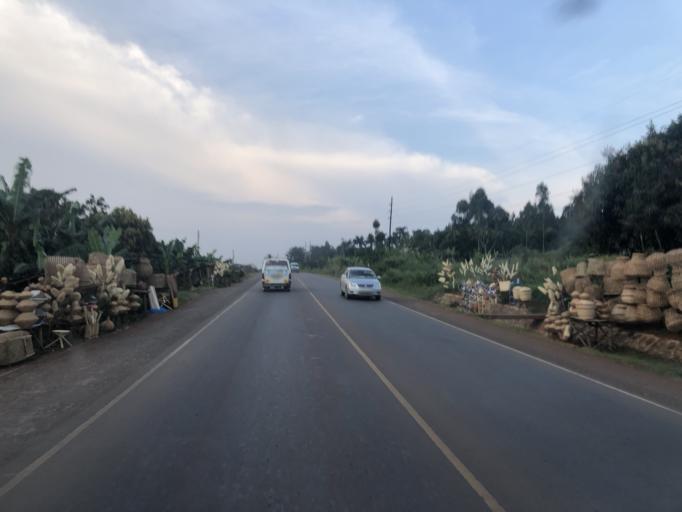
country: UG
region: Central Region
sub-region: Mpigi District
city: Mpigi
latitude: 0.2303
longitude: 32.3451
